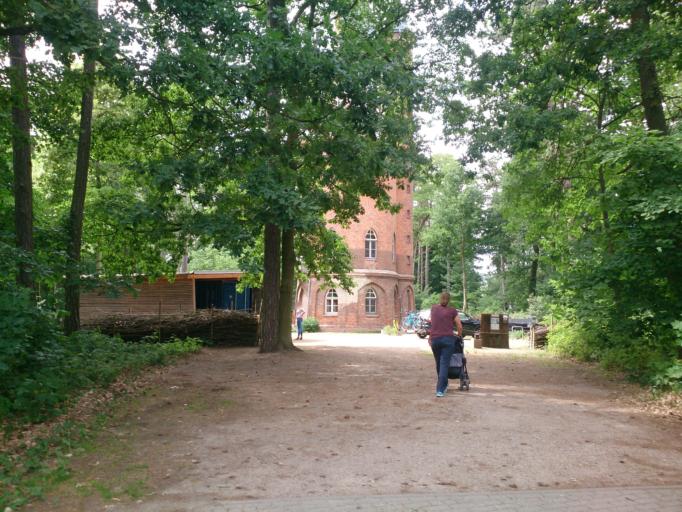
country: DE
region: Mecklenburg-Vorpommern
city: Waren
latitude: 53.5049
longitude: 12.6940
